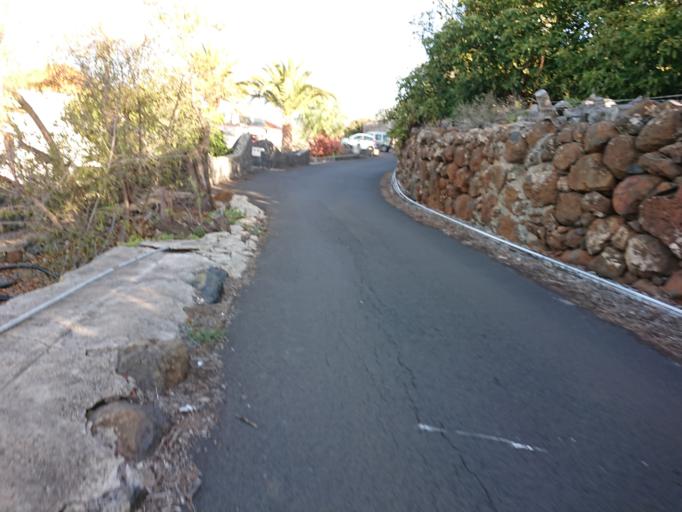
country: ES
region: Canary Islands
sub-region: Provincia de Santa Cruz de Tenerife
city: Tijarafe
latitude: 28.6792
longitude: -17.9454
